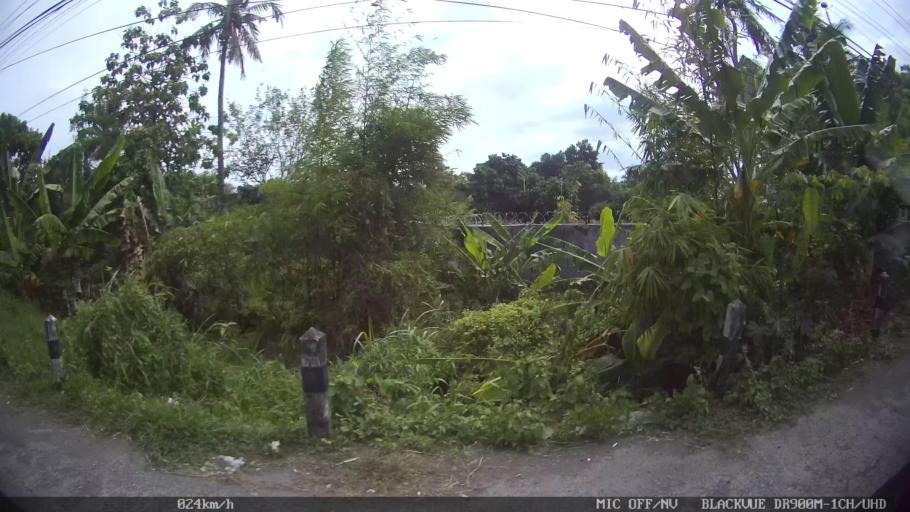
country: ID
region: Central Java
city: Candi Prambanan
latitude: -7.7342
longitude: 110.4720
